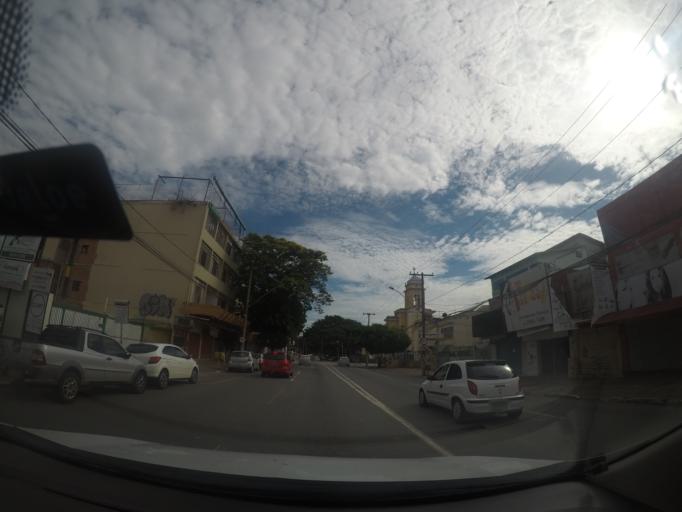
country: BR
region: Goias
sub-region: Goiania
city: Goiania
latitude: -16.6713
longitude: -49.2542
